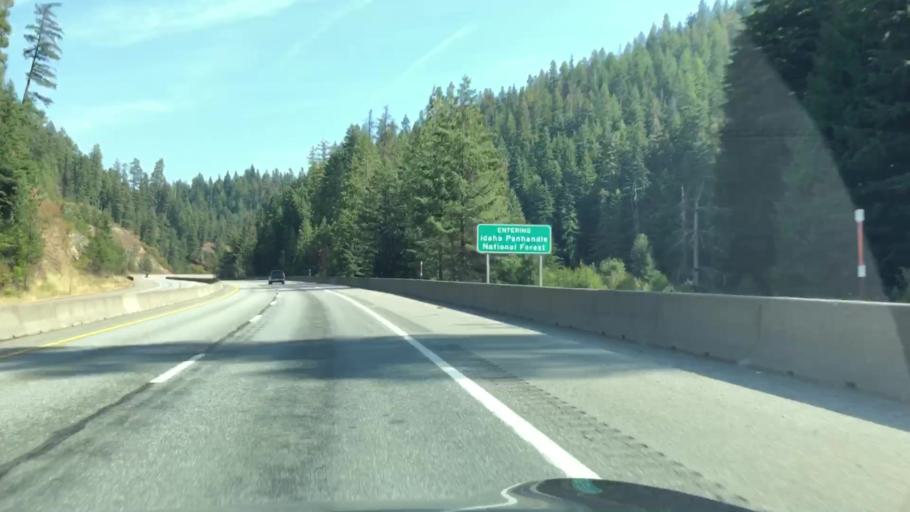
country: US
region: Idaho
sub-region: Kootenai County
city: Coeur d'Alene
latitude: 47.6280
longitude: -116.5946
